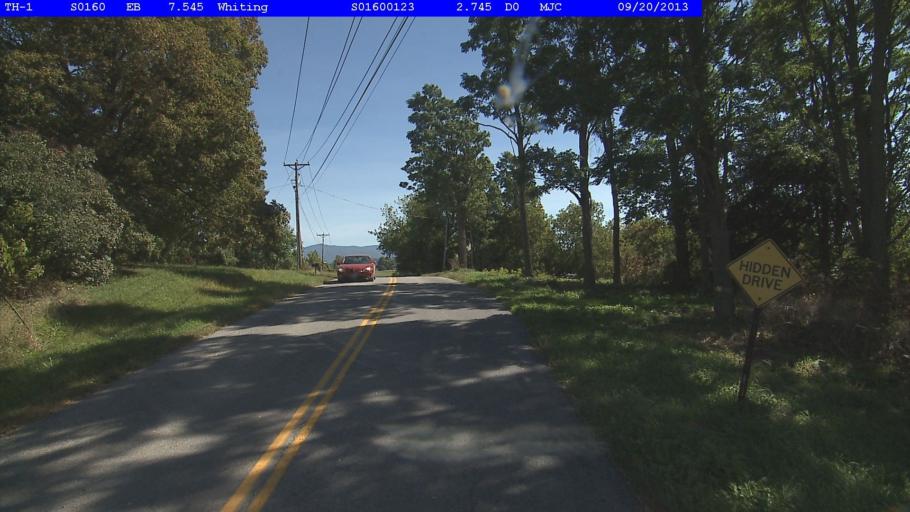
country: US
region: Vermont
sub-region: Rutland County
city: Brandon
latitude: 43.8534
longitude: -73.1756
